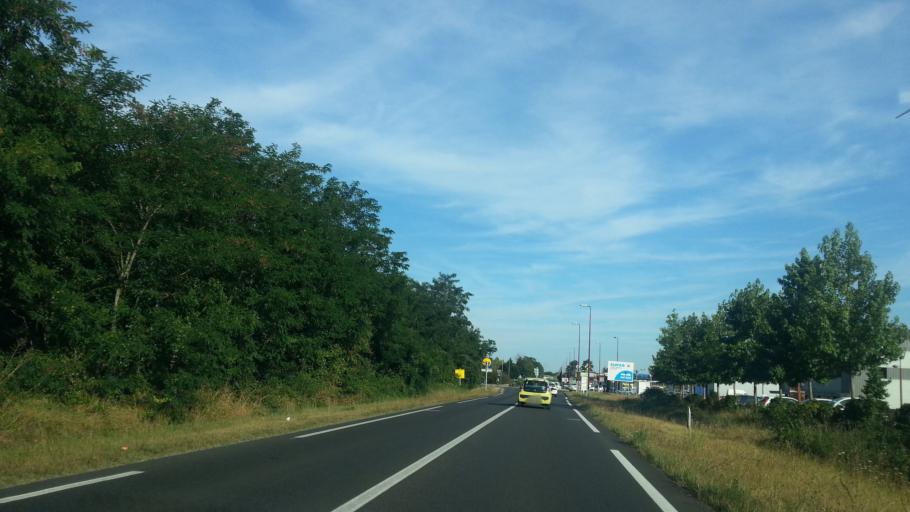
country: FR
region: Aquitaine
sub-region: Departement de la Gironde
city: Podensac
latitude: 44.6576
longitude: -0.3679
